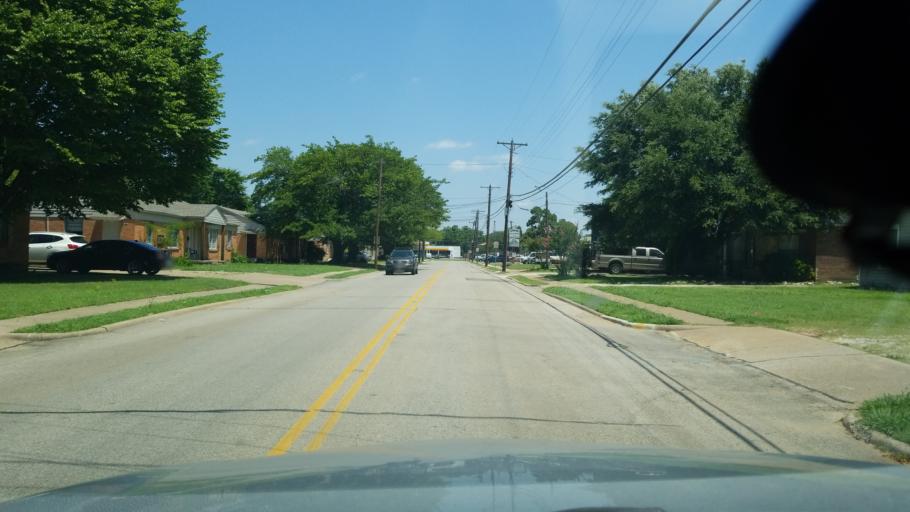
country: US
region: Texas
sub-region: Dallas County
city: Irving
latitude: 32.8204
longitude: -96.9635
